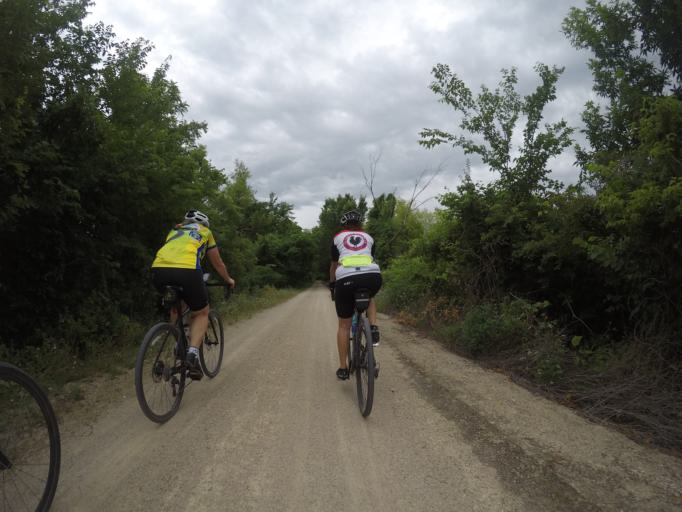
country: US
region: Kansas
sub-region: Anderson County
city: Garnett
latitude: 38.2495
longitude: -95.2536
